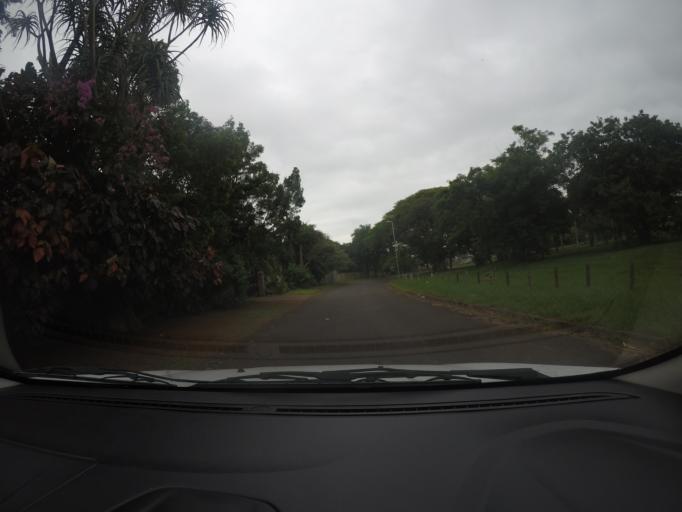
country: ZA
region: KwaZulu-Natal
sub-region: uThungulu District Municipality
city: Empangeni
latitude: -28.7628
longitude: 31.8930
